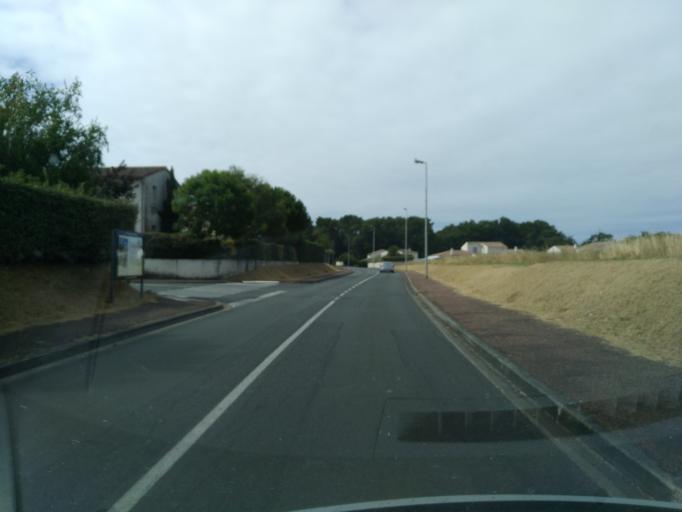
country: FR
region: Poitou-Charentes
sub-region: Departement de la Charente-Maritime
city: Saint-Palais-sur-Mer
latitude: 45.6494
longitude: -1.0859
